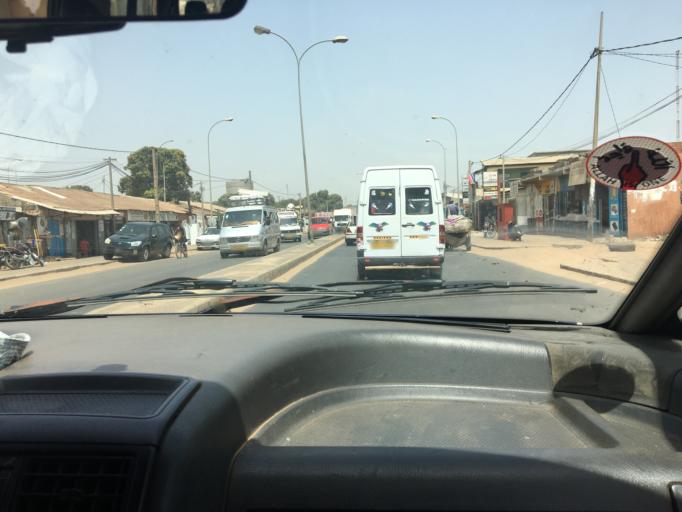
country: GM
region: Western
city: Abuko
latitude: 13.4105
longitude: -16.6697
